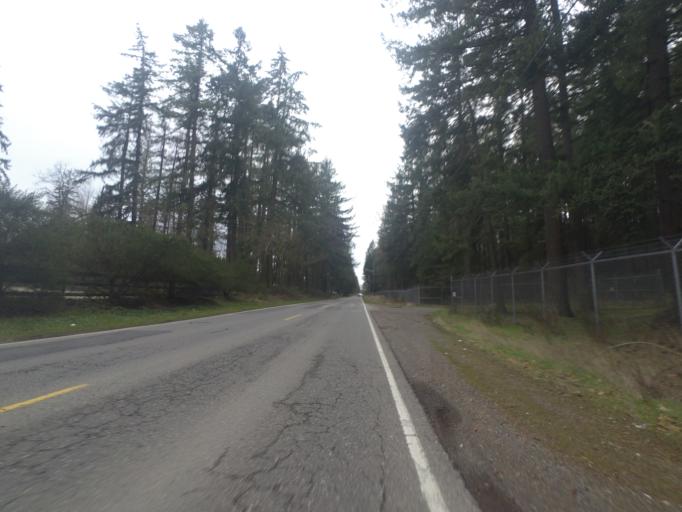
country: US
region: Washington
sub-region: Pierce County
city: McChord Air Force Base
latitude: 47.1218
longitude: -122.5162
